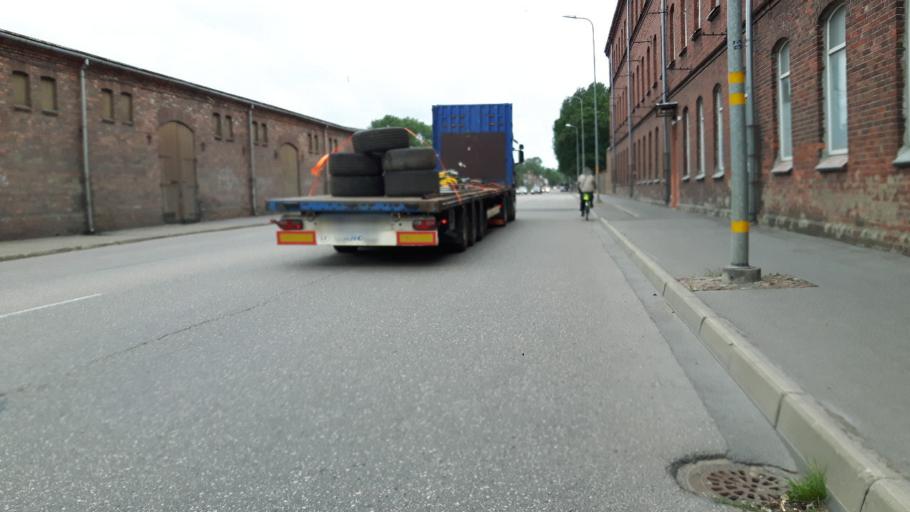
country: LV
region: Liepaja
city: Liepaja
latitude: 56.5247
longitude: 21.0042
